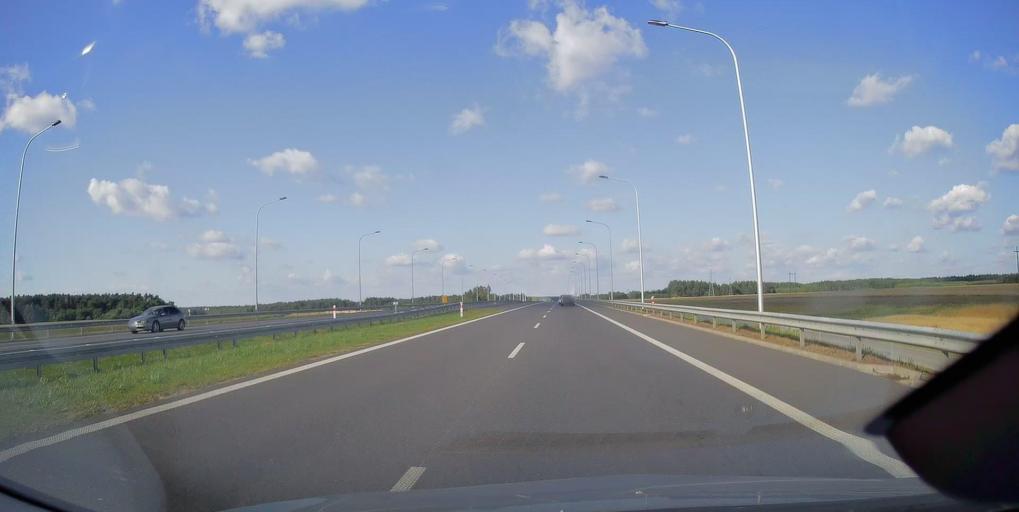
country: PL
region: Masovian Voivodeship
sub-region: Powiat szydlowiecki
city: Oronsko
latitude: 51.2928
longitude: 20.9852
